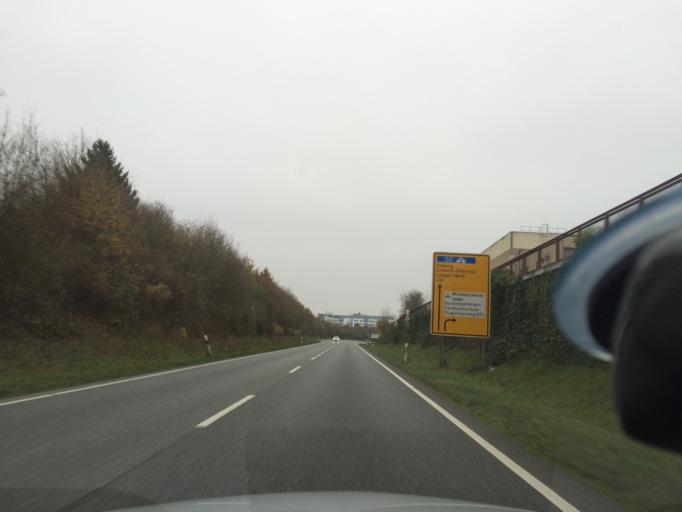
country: DE
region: Hesse
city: Langen
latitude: 49.9963
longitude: 8.6477
